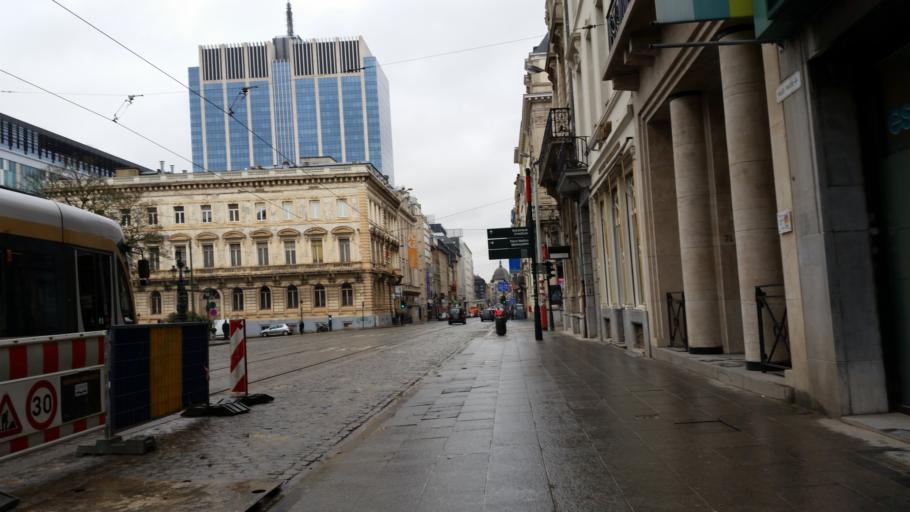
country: BE
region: Brussels Capital
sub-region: Bruxelles-Capitale
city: Brussels
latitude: 50.8494
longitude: 4.3639
